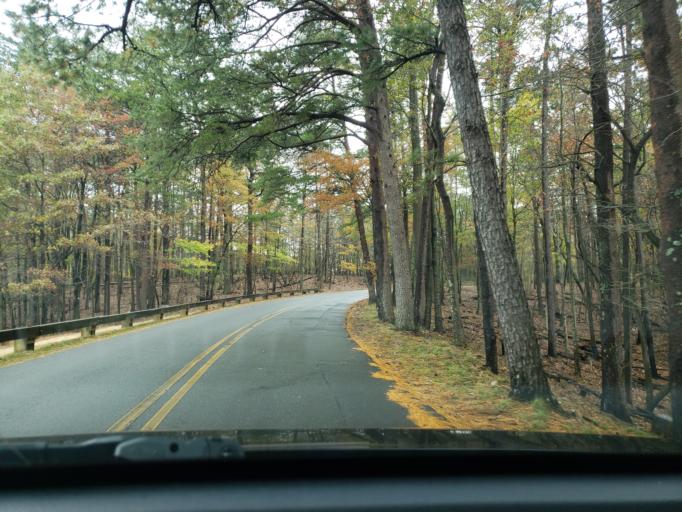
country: US
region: North Carolina
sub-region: Stokes County
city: Danbury
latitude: 36.3922
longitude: -80.2678
